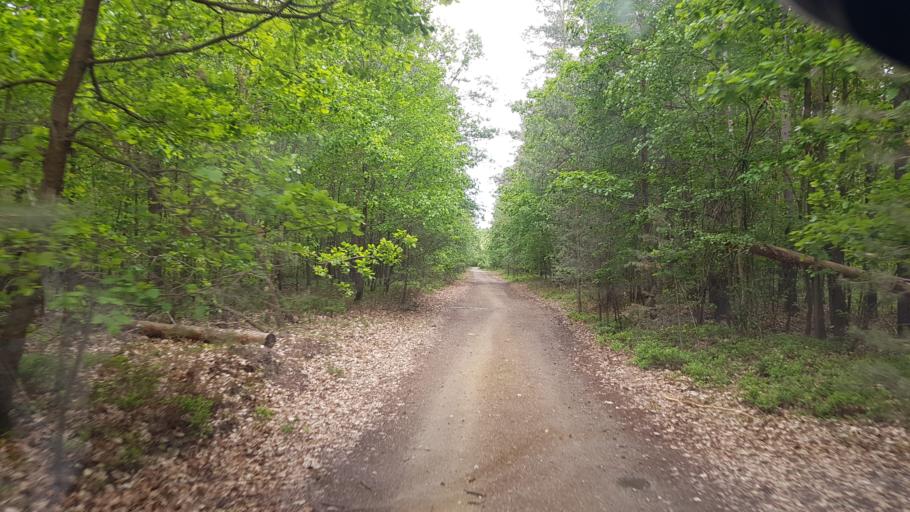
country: DE
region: Brandenburg
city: Hohenleipisch
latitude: 51.5296
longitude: 13.5405
